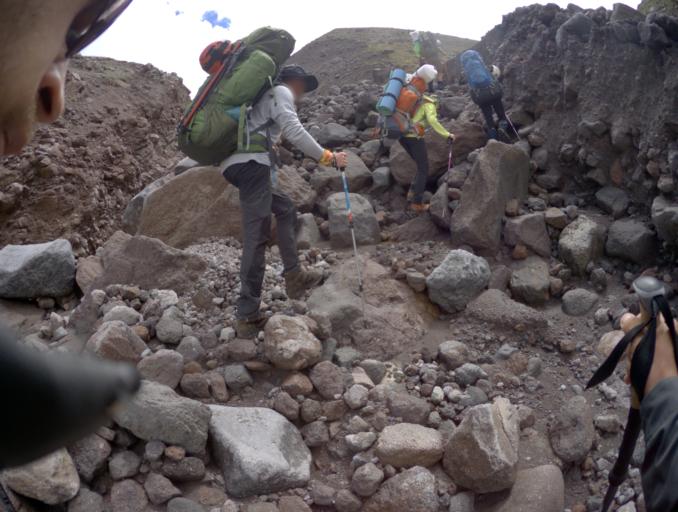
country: RU
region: Kabardino-Balkariya
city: Terskol
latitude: 43.3837
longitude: 42.3687
